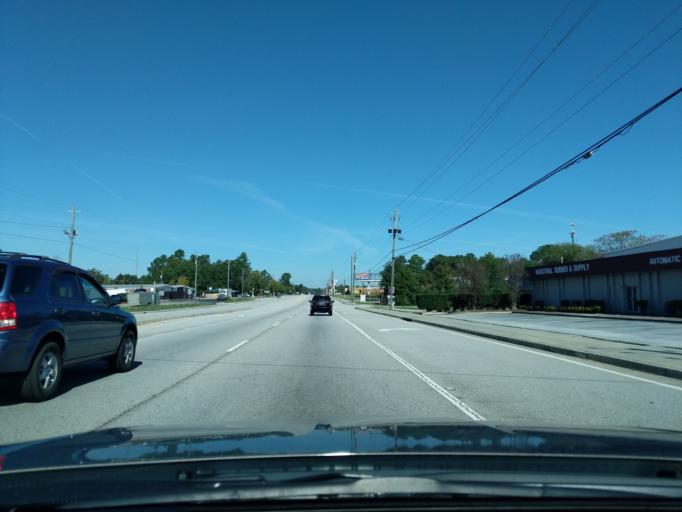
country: US
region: Georgia
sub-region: Richmond County
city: Augusta
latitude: 33.4037
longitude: -82.0060
